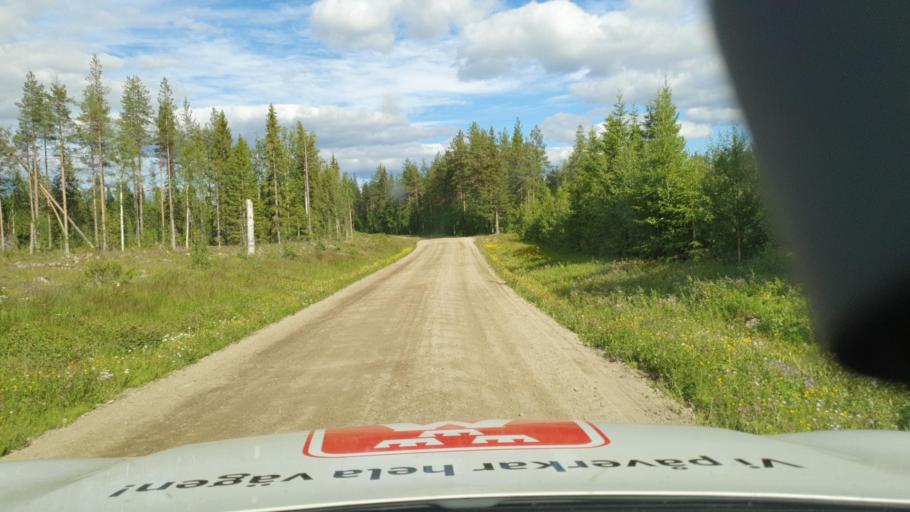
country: SE
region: Vaesterbotten
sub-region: Lycksele Kommun
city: Lycksele
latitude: 64.3298
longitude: 18.4095
